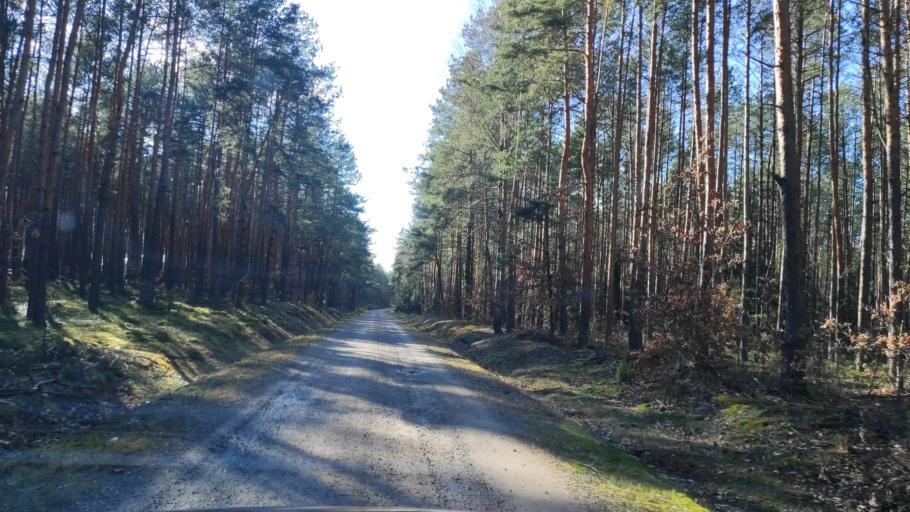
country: PL
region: Masovian Voivodeship
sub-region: Powiat radomski
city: Jastrzebia
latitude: 51.4746
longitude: 21.2560
